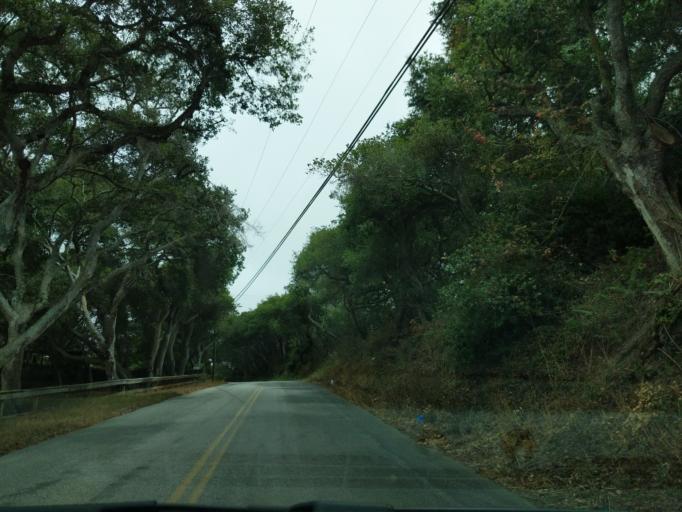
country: US
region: California
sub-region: Monterey County
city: Prunedale
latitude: 36.7889
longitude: -121.6953
